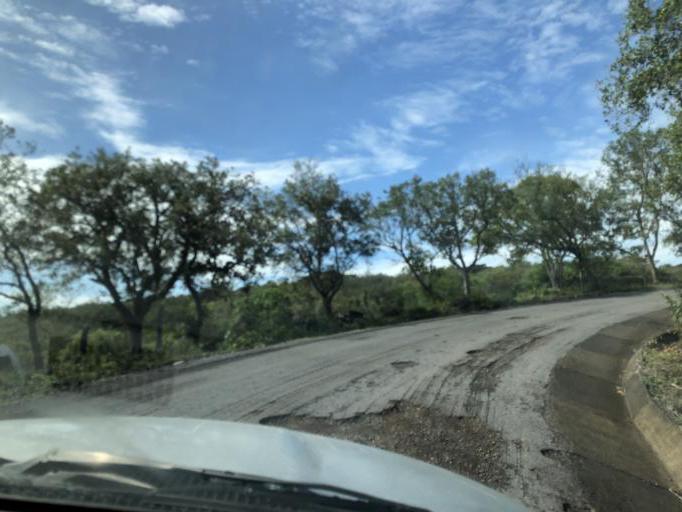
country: MX
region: Veracruz
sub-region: Alto Lucero de Gutierrez Barrios
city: Palma Sola
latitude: 19.7821
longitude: -96.5543
